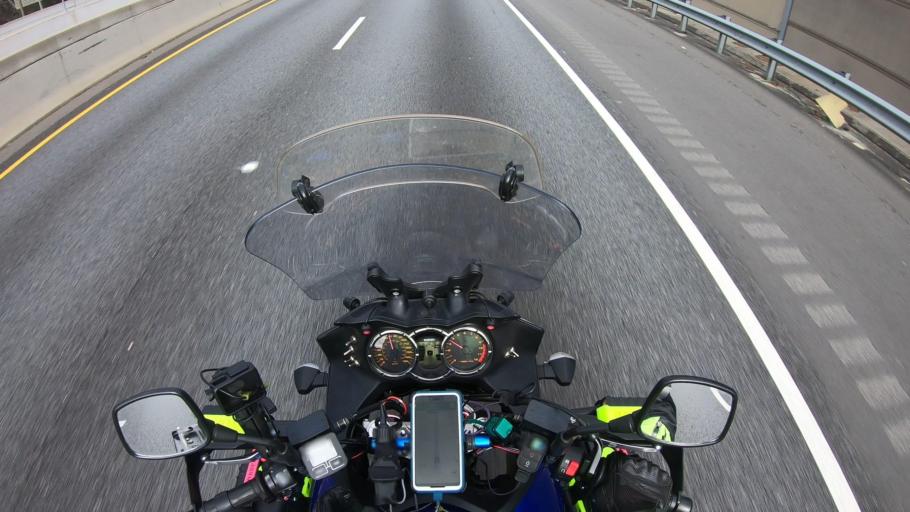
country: US
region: Georgia
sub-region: Cherokee County
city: Woodstock
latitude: 34.0621
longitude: -84.5372
